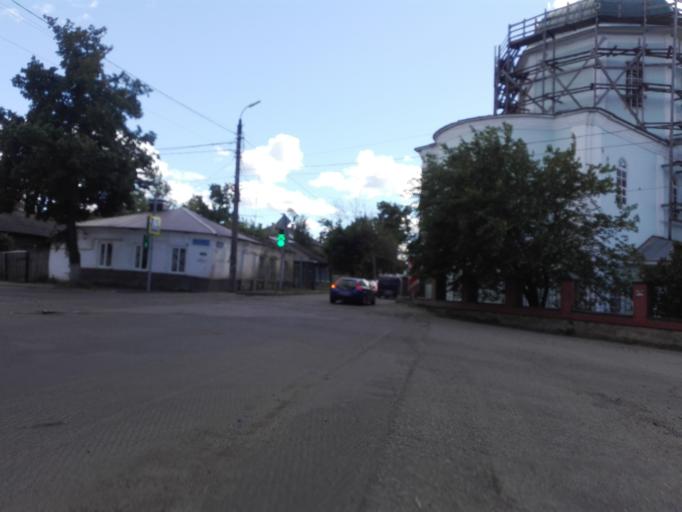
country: RU
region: Orjol
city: Orel
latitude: 52.9598
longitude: 36.0595
